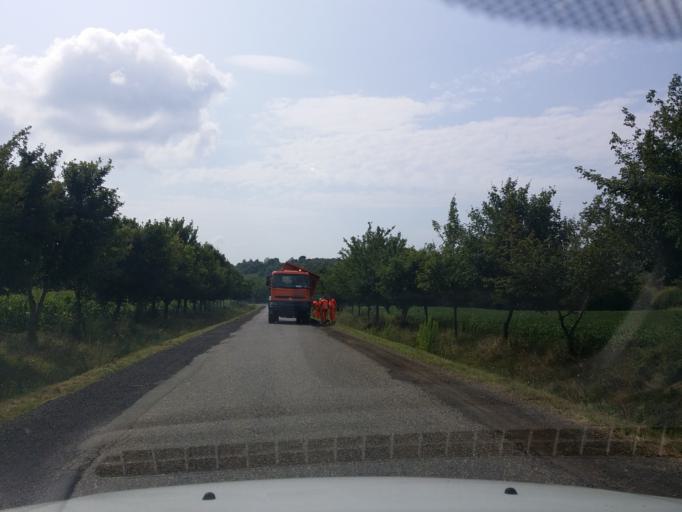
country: HU
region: Borsod-Abauj-Zemplen
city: Sarospatak
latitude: 48.4676
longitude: 21.5232
